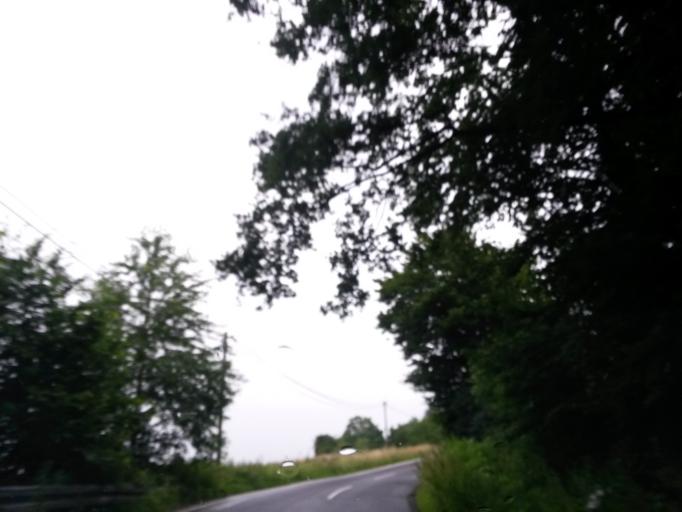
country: DE
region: North Rhine-Westphalia
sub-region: Regierungsbezirk Koln
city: Much
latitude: 50.9476
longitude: 7.3654
